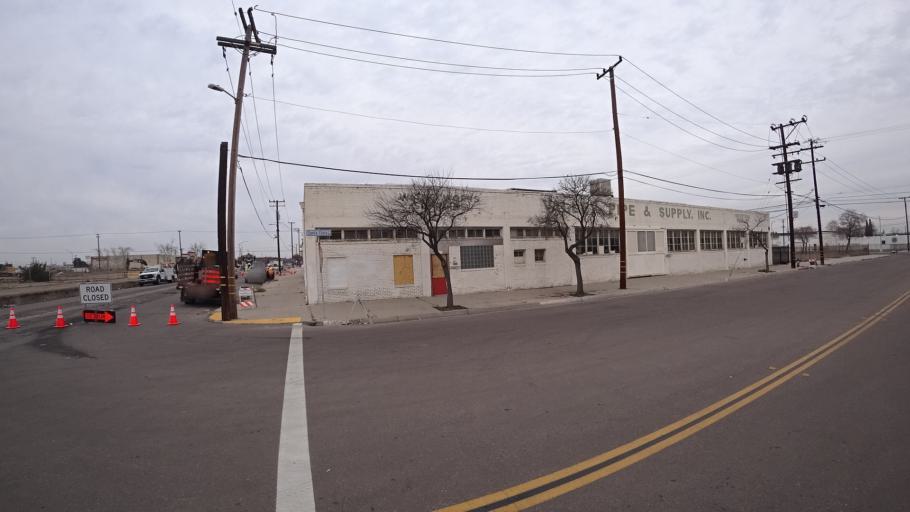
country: US
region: California
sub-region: Fresno County
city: Fresno
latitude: 36.7275
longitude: -119.7866
